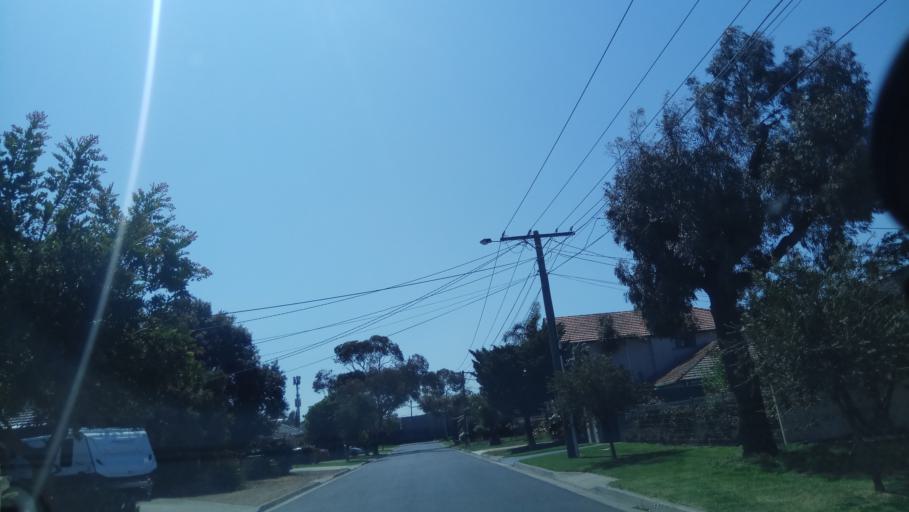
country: AU
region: Victoria
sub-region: Wyndham
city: Williams Landing
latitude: -37.8711
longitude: 144.7552
